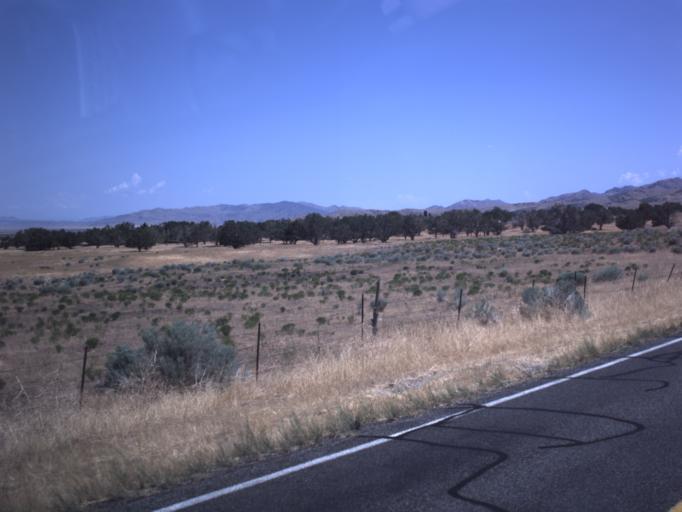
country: US
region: Utah
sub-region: Millard County
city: Delta
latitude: 39.3626
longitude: -112.3487
